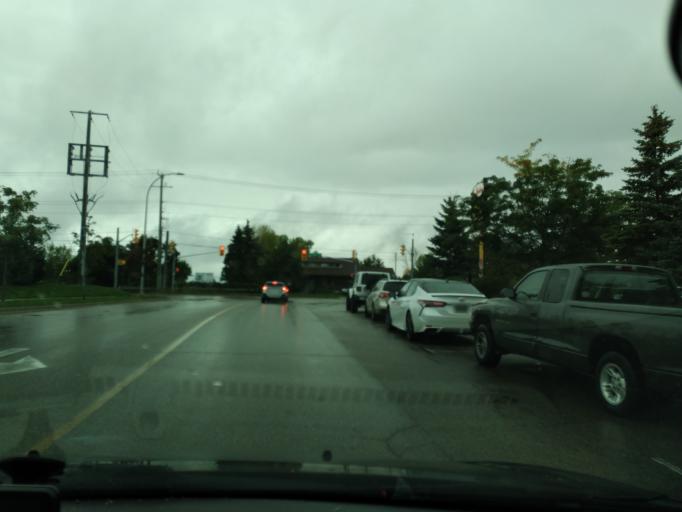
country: CA
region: Ontario
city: Barrie
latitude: 44.4160
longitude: -79.6591
